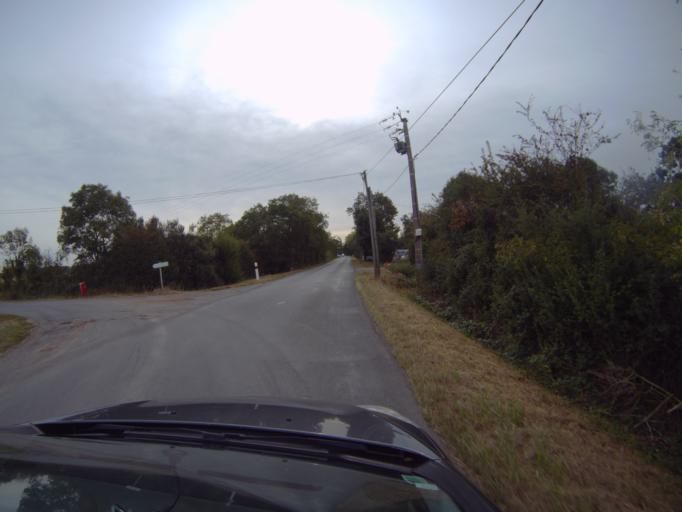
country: FR
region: Pays de la Loire
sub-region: Departement de la Vendee
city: Angles
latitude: 46.4071
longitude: -1.4231
